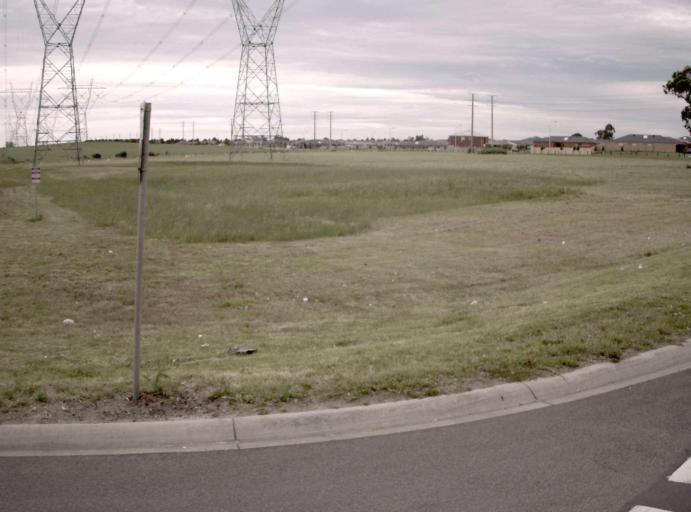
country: AU
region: Victoria
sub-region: Casey
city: Cranbourne North
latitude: -38.0888
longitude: 145.2794
